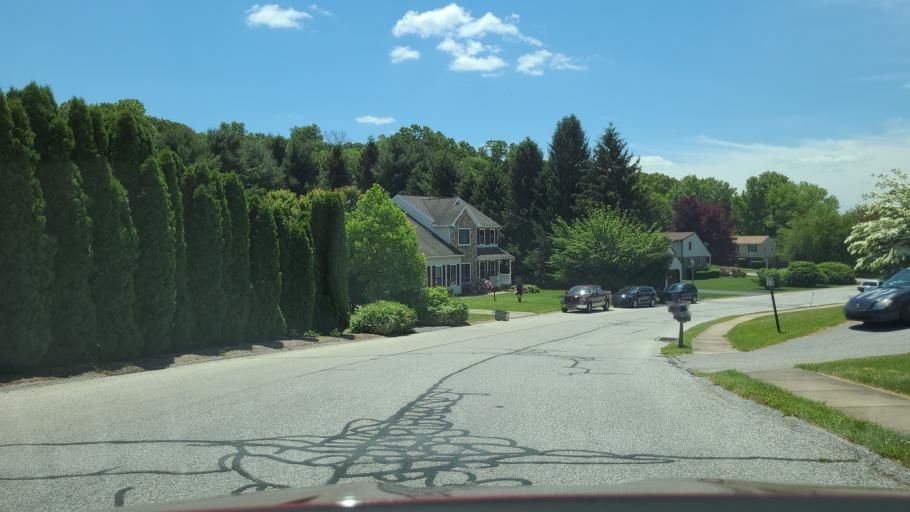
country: US
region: Pennsylvania
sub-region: York County
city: New Freedom
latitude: 39.7369
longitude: -76.6911
